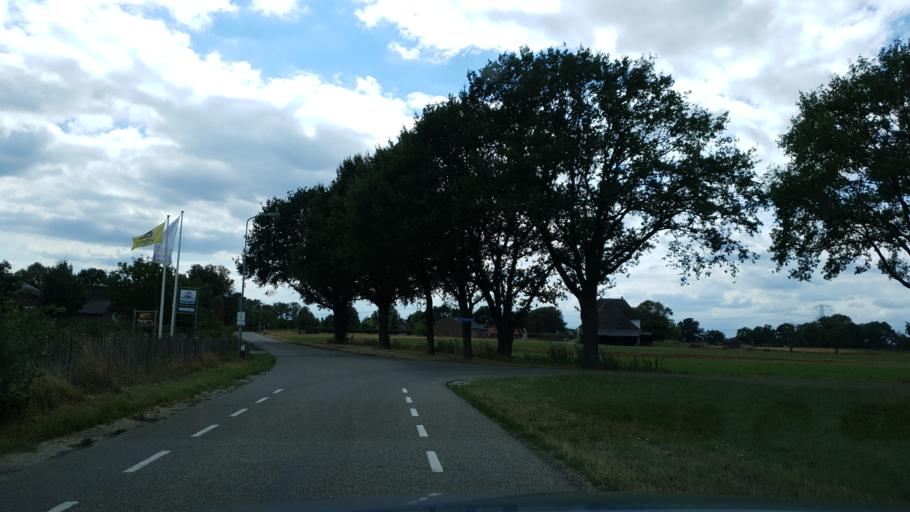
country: NL
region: Gelderland
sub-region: Gemeente Nijmegen
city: Lindenholt
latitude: 51.7687
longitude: 5.8065
